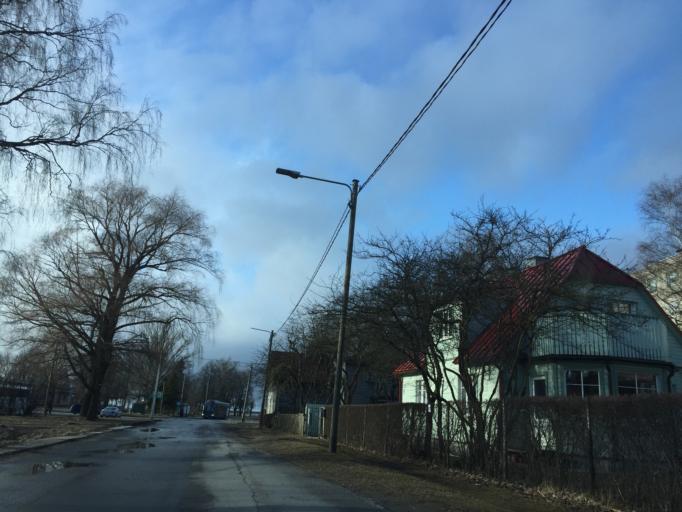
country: EE
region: Laeaene
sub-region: Haapsalu linn
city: Haapsalu
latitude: 58.9374
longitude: 23.5346
